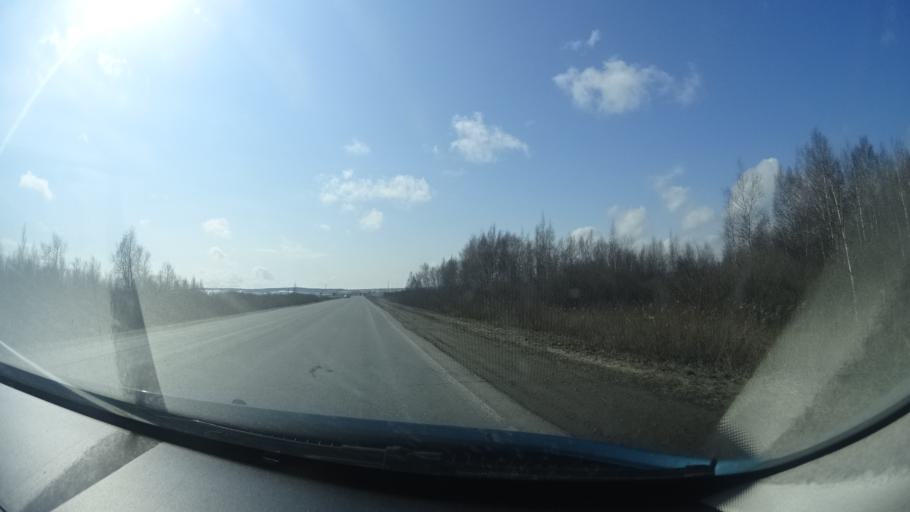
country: RU
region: Bashkortostan
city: Mikhaylovka
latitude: 54.8988
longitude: 55.7250
